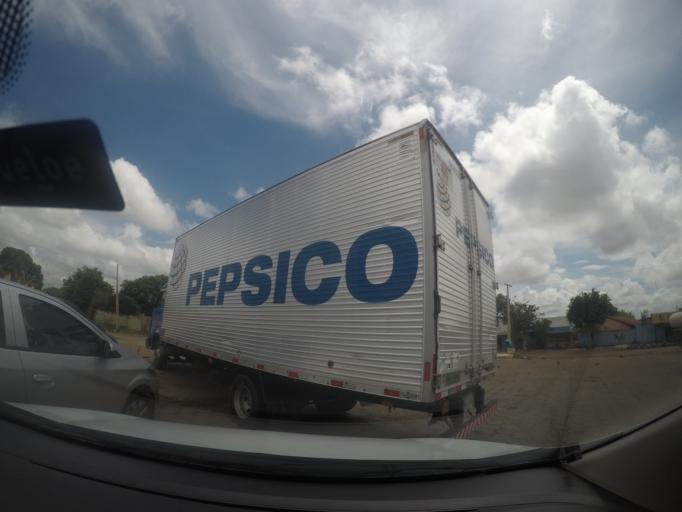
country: BR
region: Goias
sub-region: Goiania
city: Goiania
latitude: -16.7211
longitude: -49.3739
